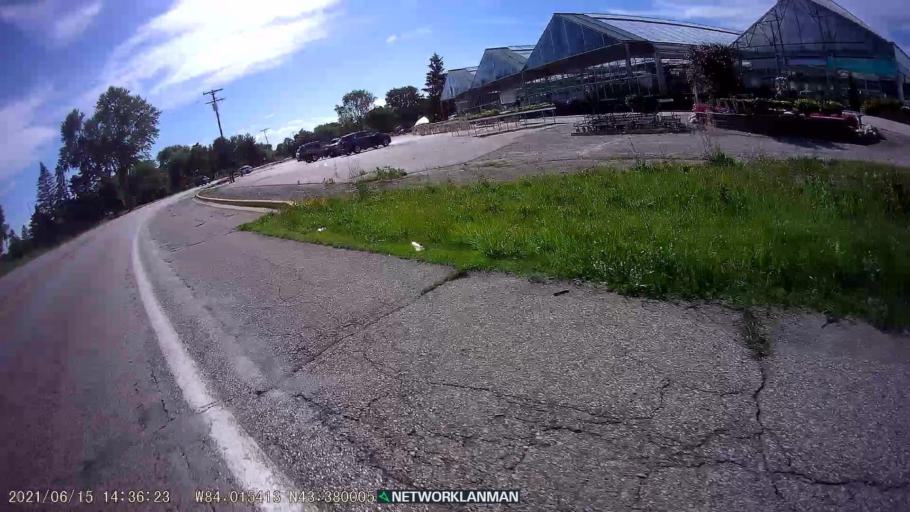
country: US
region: Michigan
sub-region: Saginaw County
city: Shields
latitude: 43.3794
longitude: -84.0153
